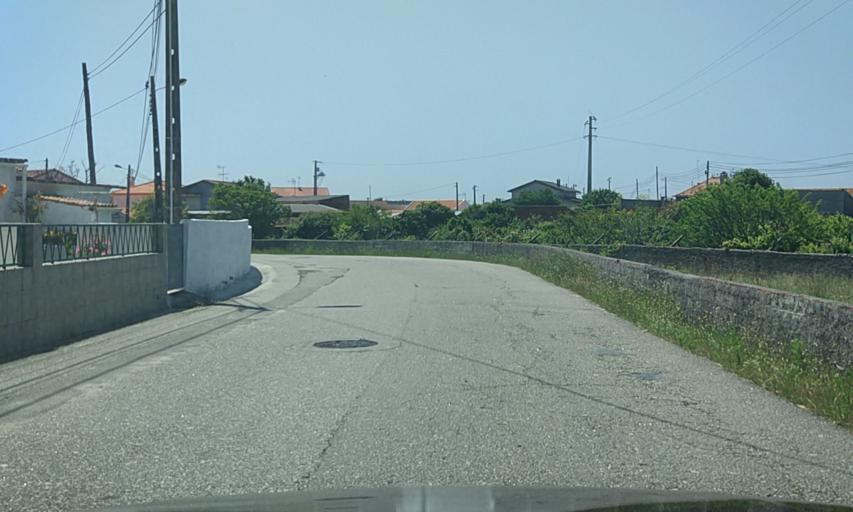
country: PT
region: Aveiro
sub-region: Aveiro
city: Aveiro
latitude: 40.6441
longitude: -8.6192
